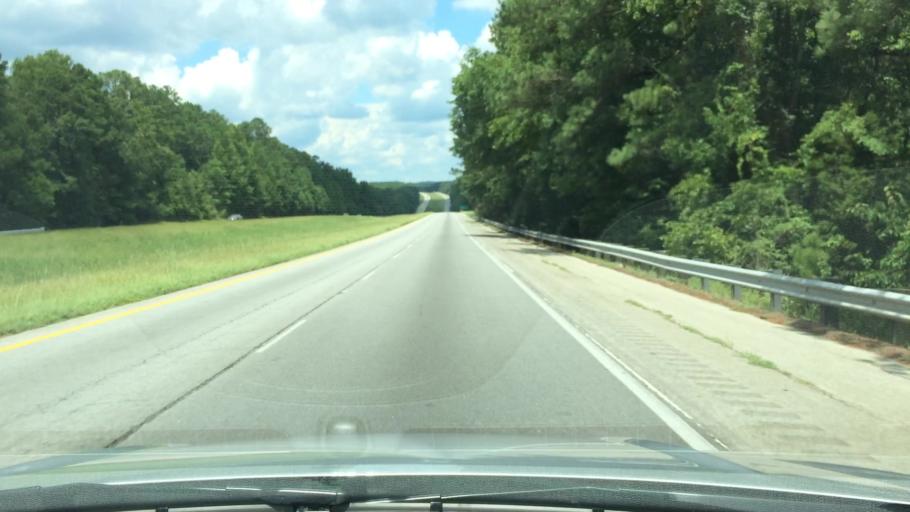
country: US
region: South Carolina
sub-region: Laurens County
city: Joanna
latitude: 34.3863
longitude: -81.6856
